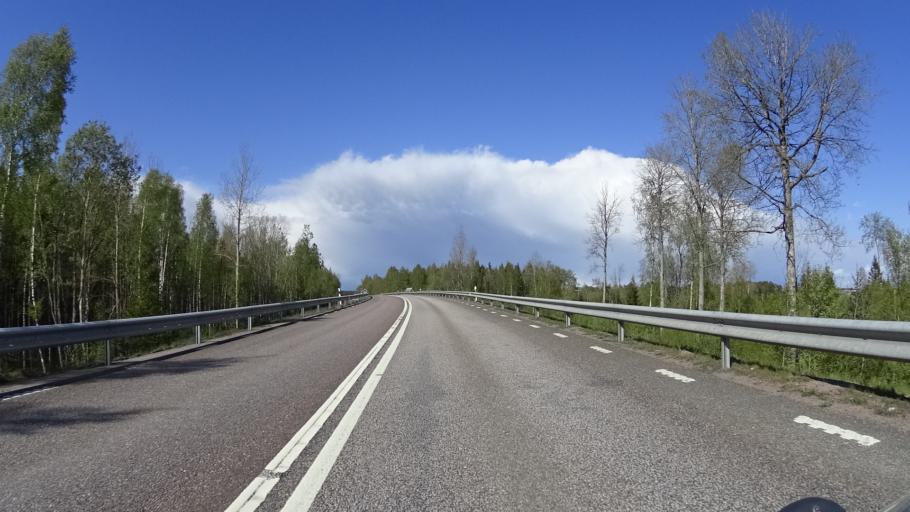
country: SE
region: Vaestra Goetaland
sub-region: Karlsborgs Kommun
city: Karlsborg
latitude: 58.5016
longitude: 14.4632
